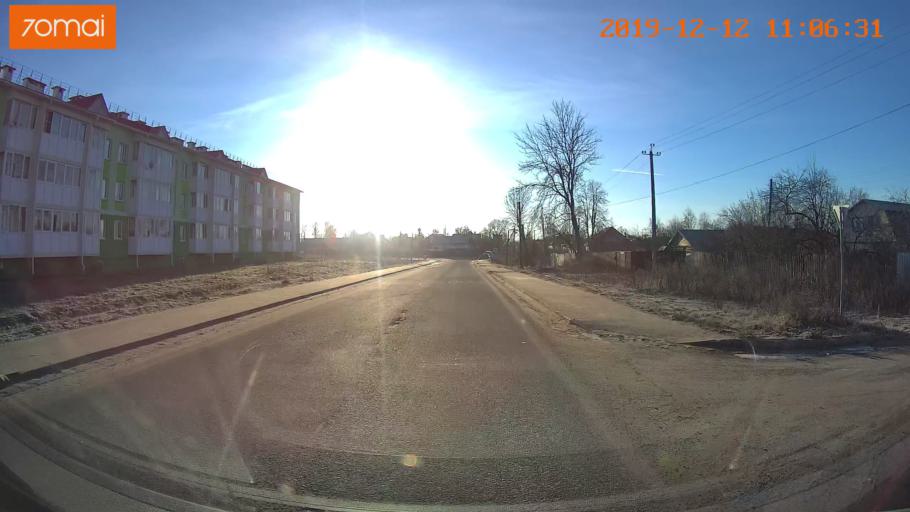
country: RU
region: Ivanovo
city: Kokhma
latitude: 56.9435
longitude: 41.0884
